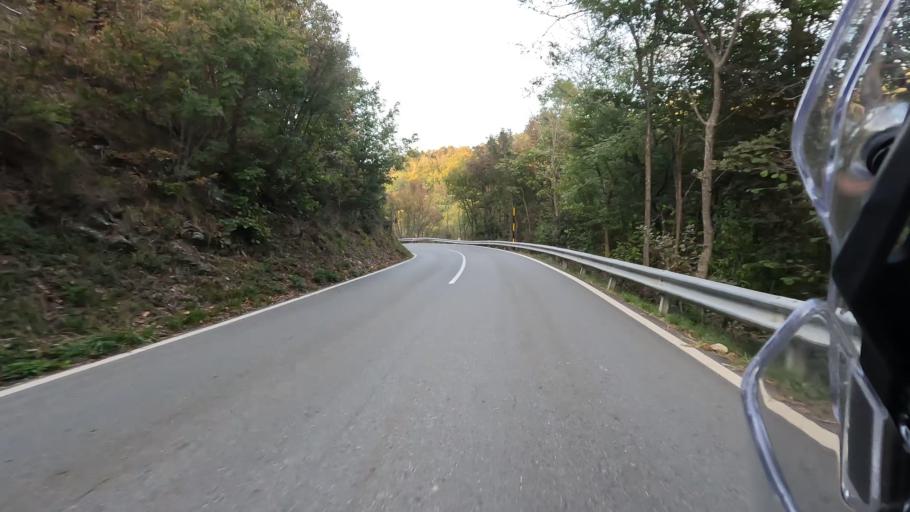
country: IT
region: Liguria
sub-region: Provincia di Savona
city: Sassello
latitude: 44.5072
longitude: 8.4825
